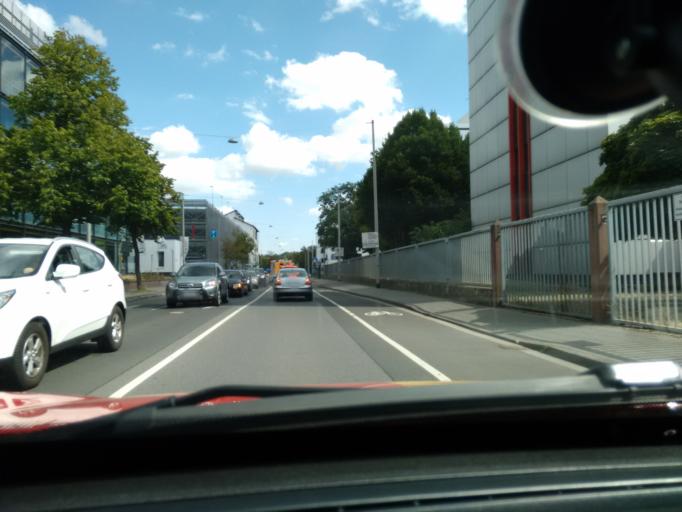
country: DE
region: Rheinland-Pfalz
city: Mainz
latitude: 49.9887
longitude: 8.2687
